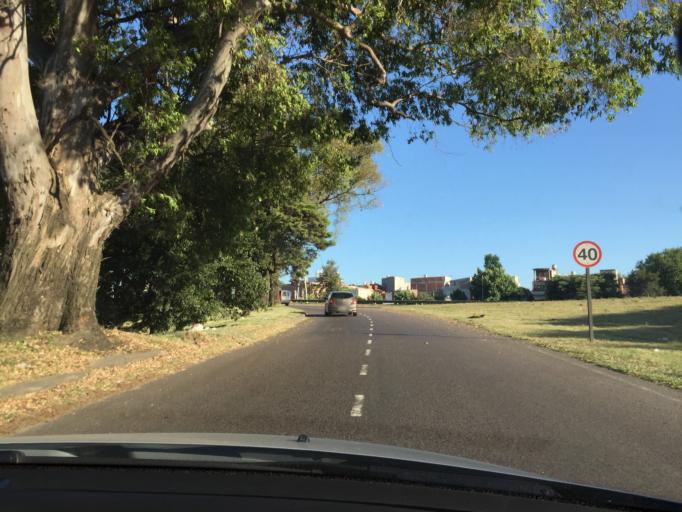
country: AR
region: Buenos Aires F.D.
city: Villa Lugano
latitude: -34.6861
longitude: -58.4857
